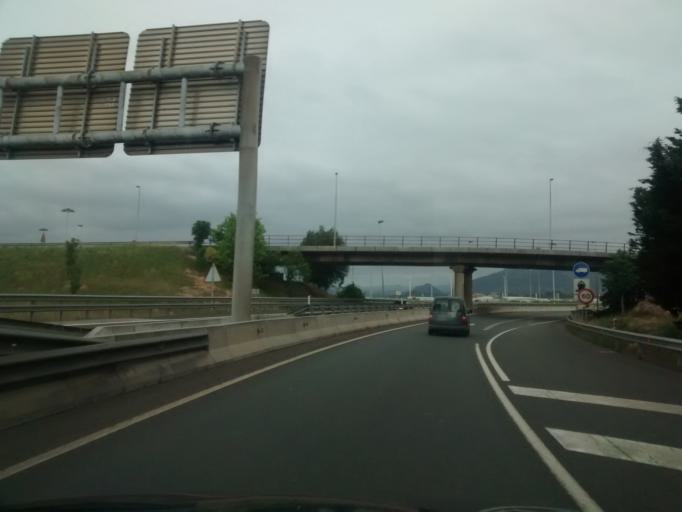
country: ES
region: Cantabria
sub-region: Provincia de Cantabria
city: Santander
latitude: 43.4400
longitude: -3.8339
